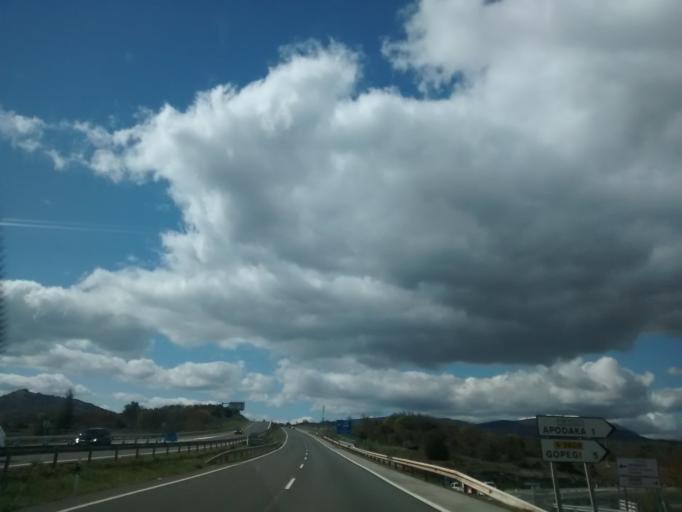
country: ES
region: Basque Country
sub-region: Provincia de Alava
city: Gasteiz / Vitoria
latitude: 42.9236
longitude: -2.7297
